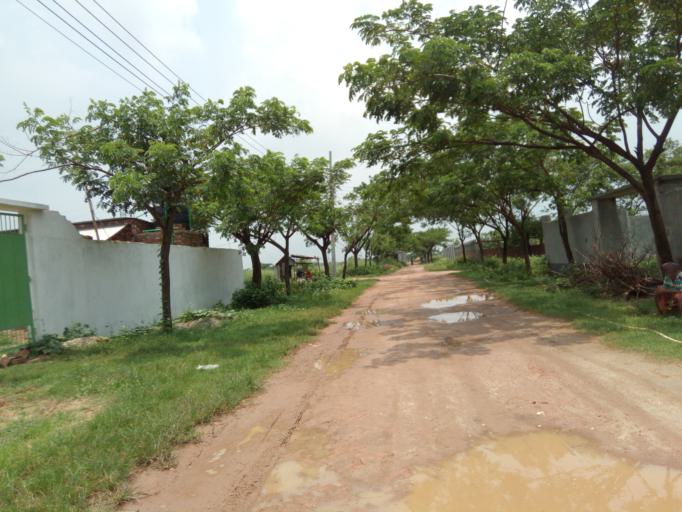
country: BD
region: Dhaka
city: Azimpur
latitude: 23.7518
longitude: 90.3356
